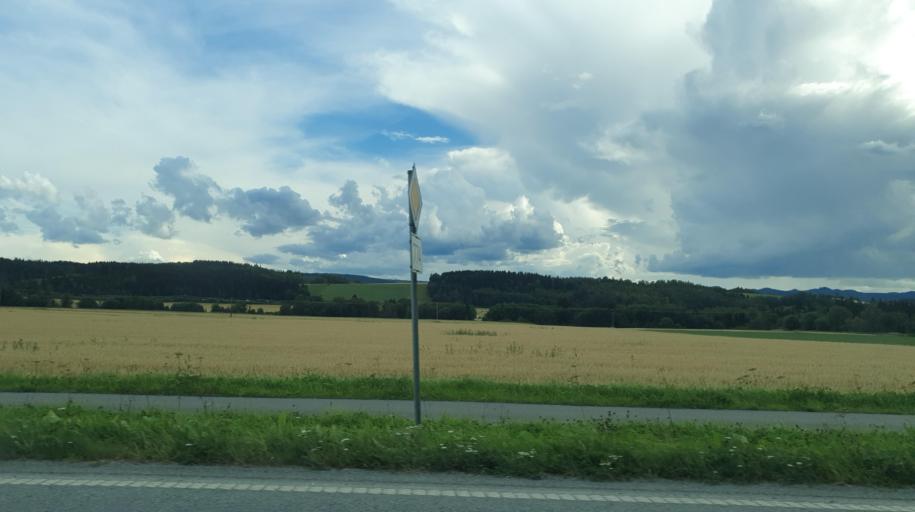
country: NO
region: Nord-Trondelag
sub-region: Levanger
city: Levanger
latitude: 63.7533
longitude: 11.3622
